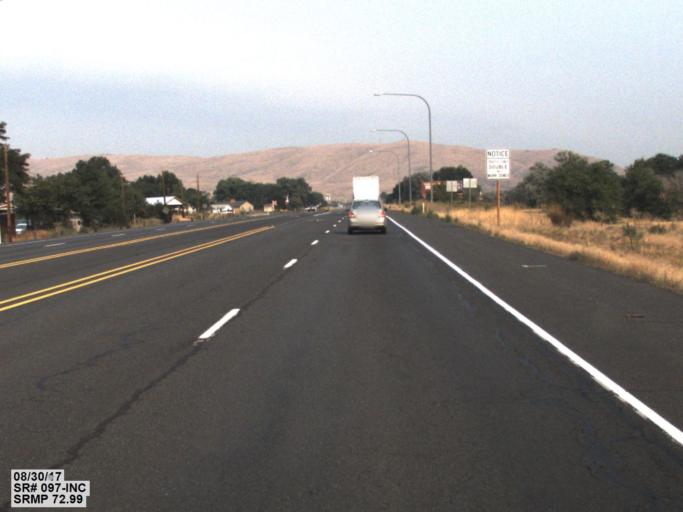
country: US
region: Washington
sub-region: Yakima County
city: Union Gap
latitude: 46.4987
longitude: -120.4633
